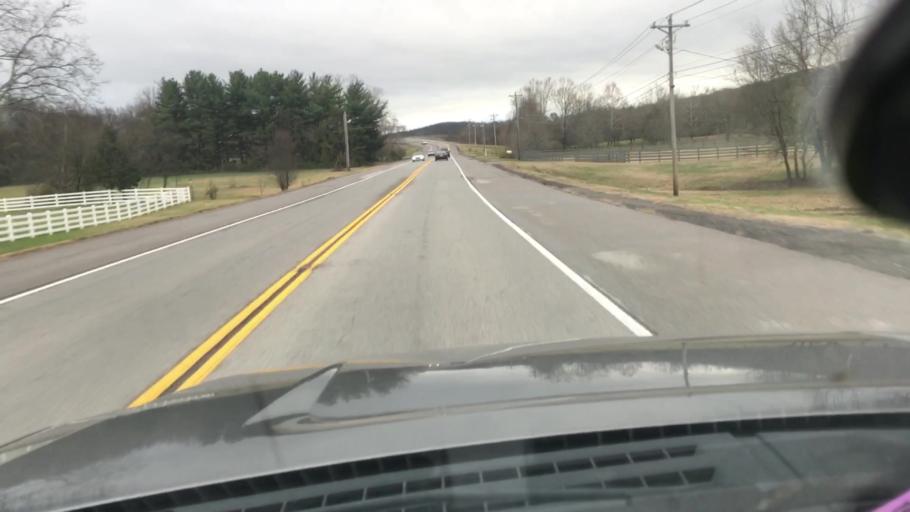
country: US
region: Tennessee
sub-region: Williamson County
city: Brentwood Estates
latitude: 35.9648
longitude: -86.7720
